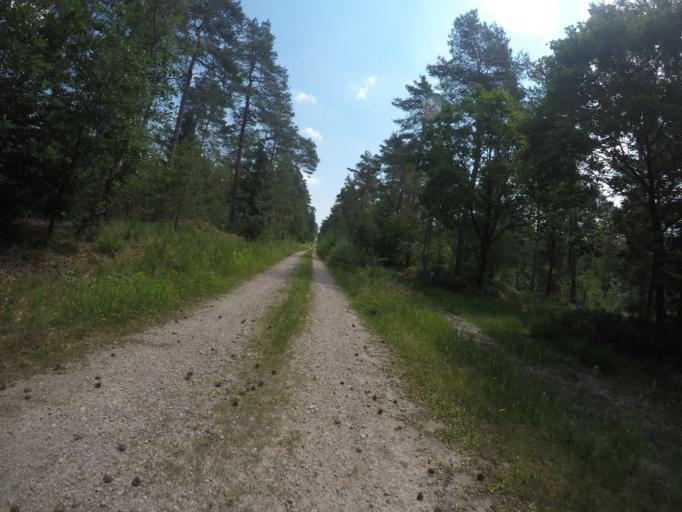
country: DE
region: Lower Saxony
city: Jesteburg
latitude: 53.2577
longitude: 9.9336
